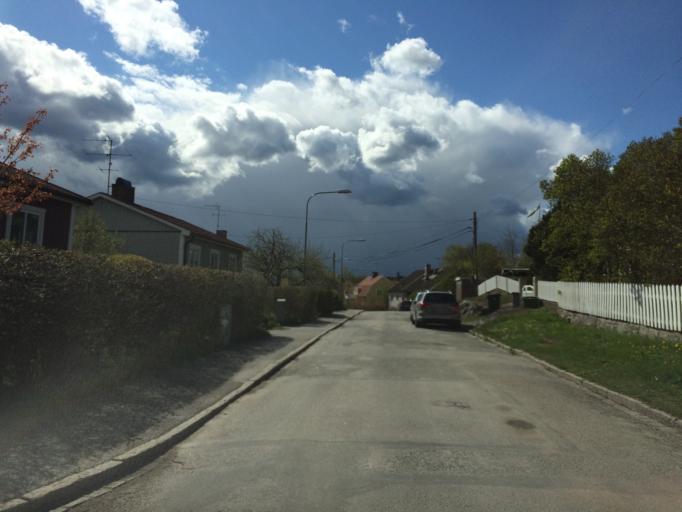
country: SE
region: Stockholm
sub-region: Huddinge Kommun
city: Segeltorp
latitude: 59.2932
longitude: 17.9547
